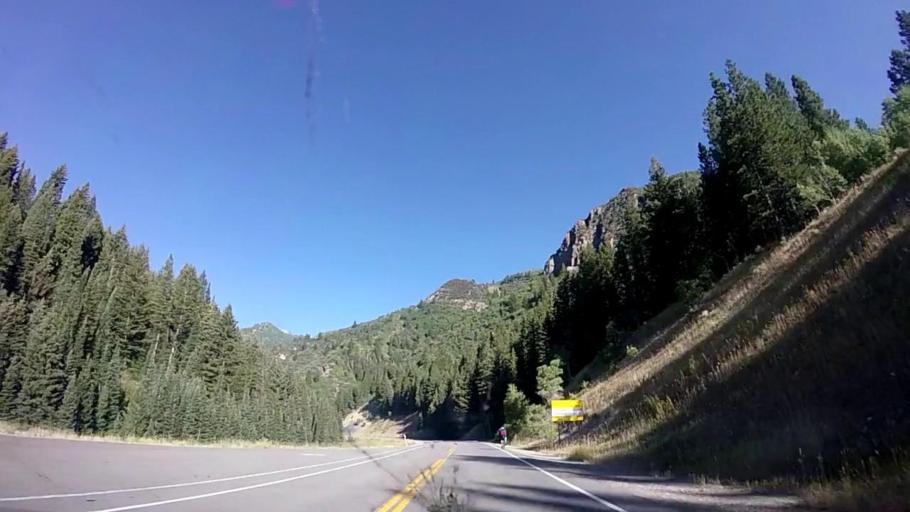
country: US
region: Utah
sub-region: Summit County
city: Summit Park
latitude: 40.6505
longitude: -111.6499
